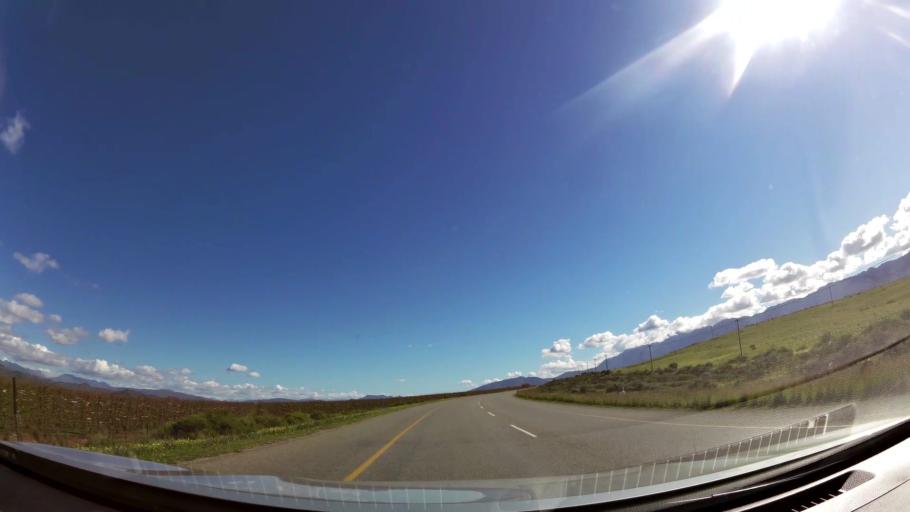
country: ZA
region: Western Cape
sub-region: Cape Winelands District Municipality
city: Ashton
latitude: -33.8392
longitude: 20.0100
